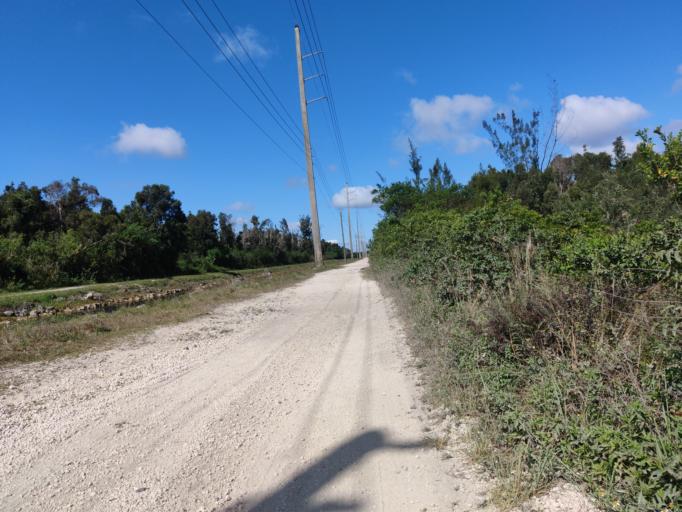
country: US
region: Florida
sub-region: Miami-Dade County
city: Kendall West
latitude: 25.7274
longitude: -80.4694
